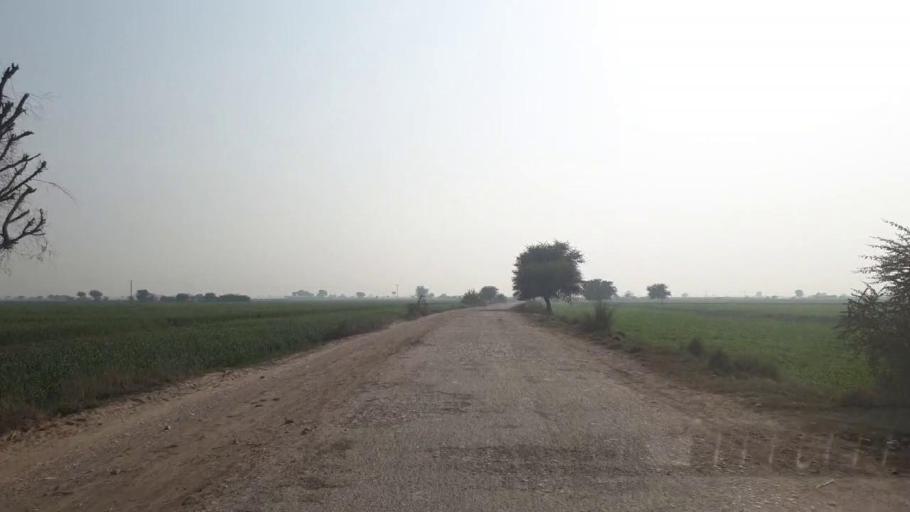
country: PK
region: Sindh
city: Hala
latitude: 25.7618
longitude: 68.3849
